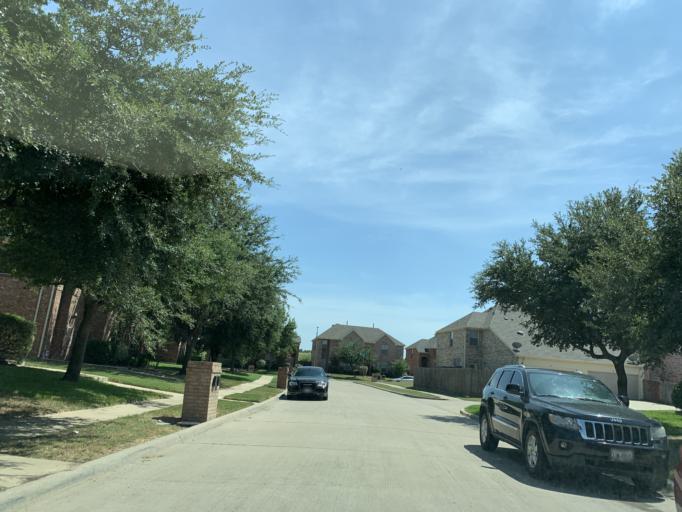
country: US
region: Texas
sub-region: Dallas County
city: Cedar Hill
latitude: 32.6424
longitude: -97.0189
